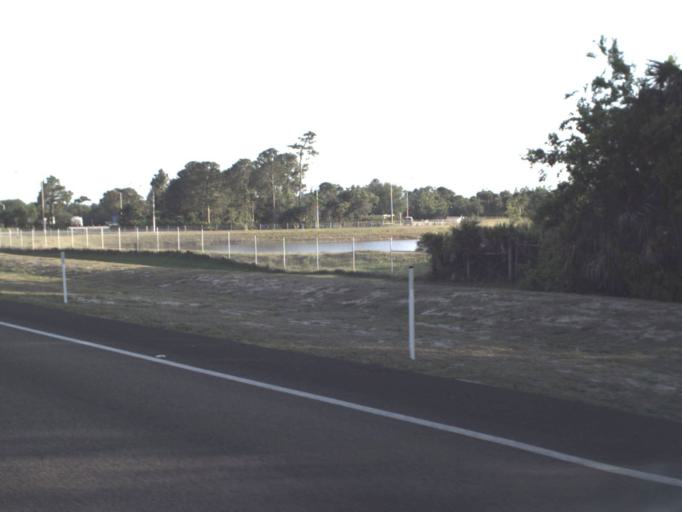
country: US
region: Florida
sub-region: Brevard County
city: Mims
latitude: 28.7116
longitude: -80.8886
